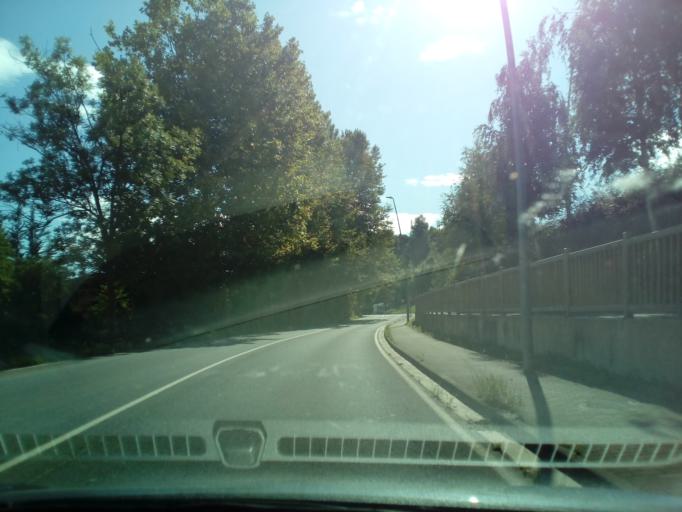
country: ES
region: Basque Country
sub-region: Provincia de Guipuzcoa
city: Andoain
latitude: 43.2092
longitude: -2.0370
